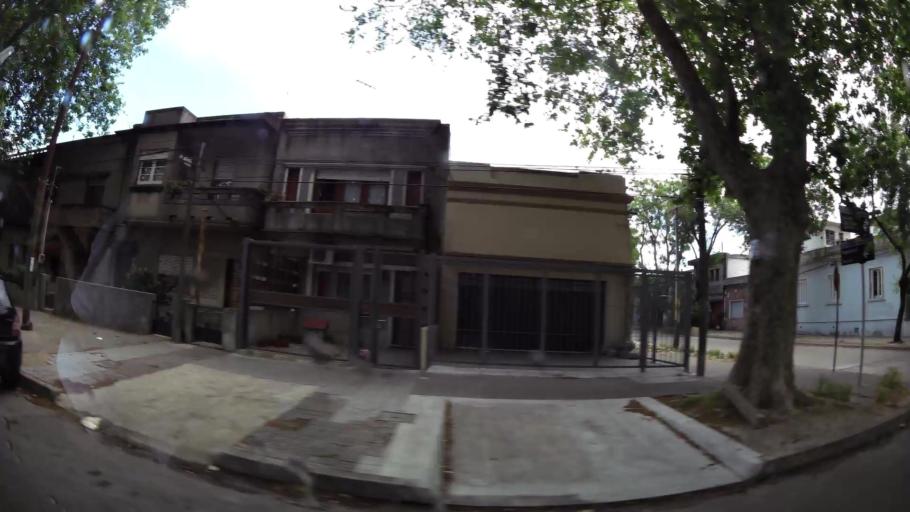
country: UY
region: Montevideo
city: Montevideo
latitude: -34.8650
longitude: -56.1800
